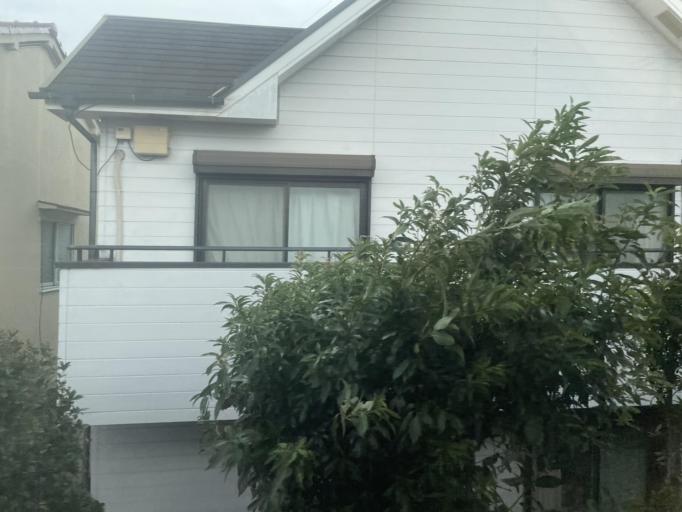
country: JP
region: Hyogo
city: Ashiya
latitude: 34.7255
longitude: 135.2618
